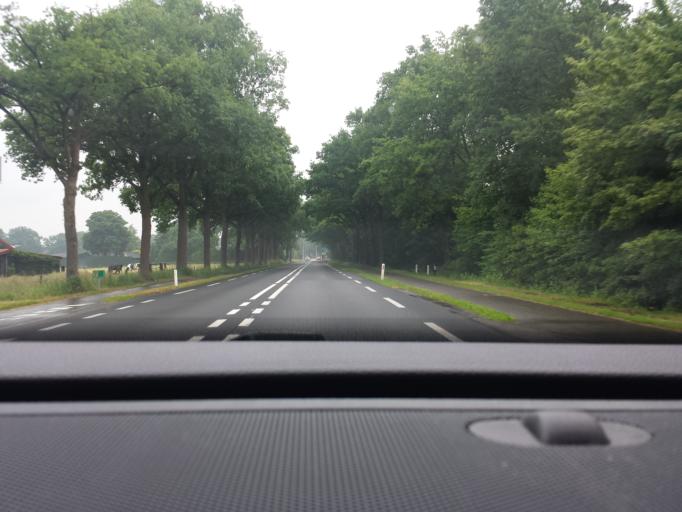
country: NL
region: Overijssel
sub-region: Gemeente Enschede
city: Enschede
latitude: 52.1985
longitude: 6.8305
